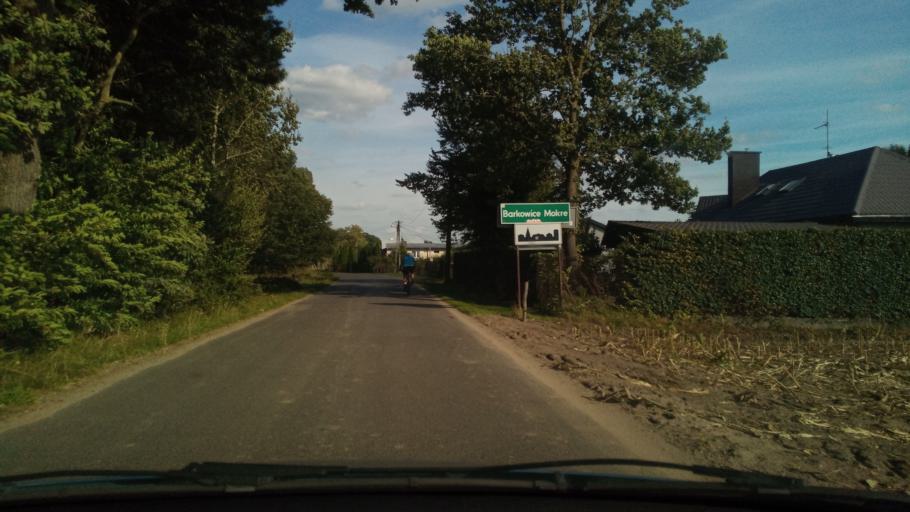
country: PL
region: Lodz Voivodeship
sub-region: Powiat piotrkowski
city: Sulejow
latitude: 51.4067
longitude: 19.8554
